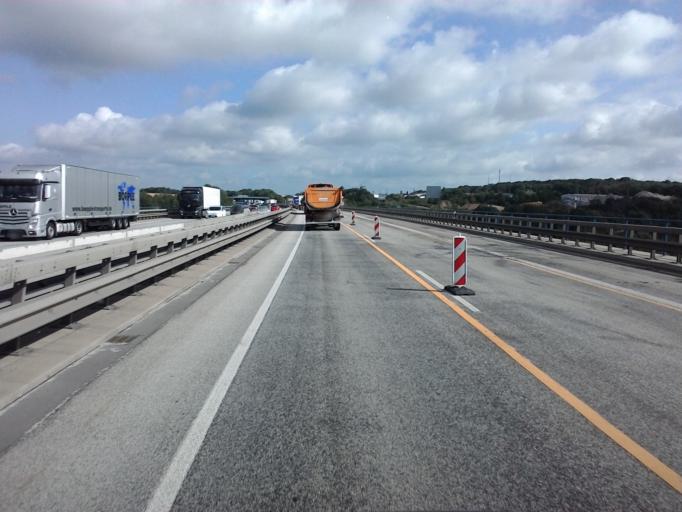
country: DE
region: Rheinland-Pfalz
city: Niederzissen
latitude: 50.4612
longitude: 7.2342
